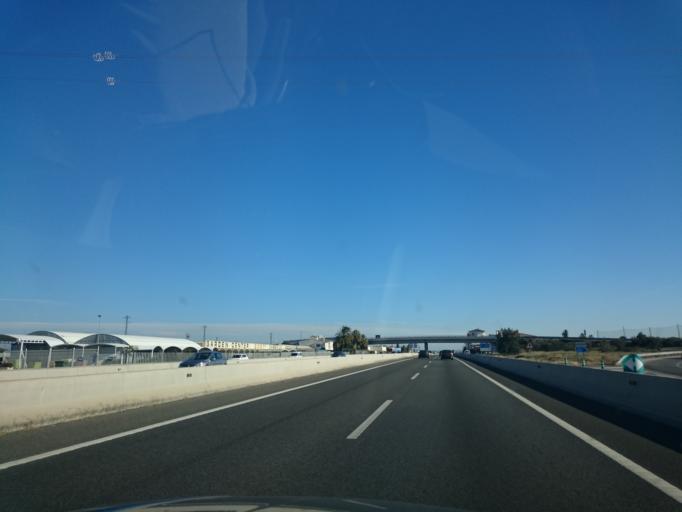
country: ES
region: Catalonia
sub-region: Provincia de Tarragona
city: Cambrils
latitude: 41.0878
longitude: 1.0884
